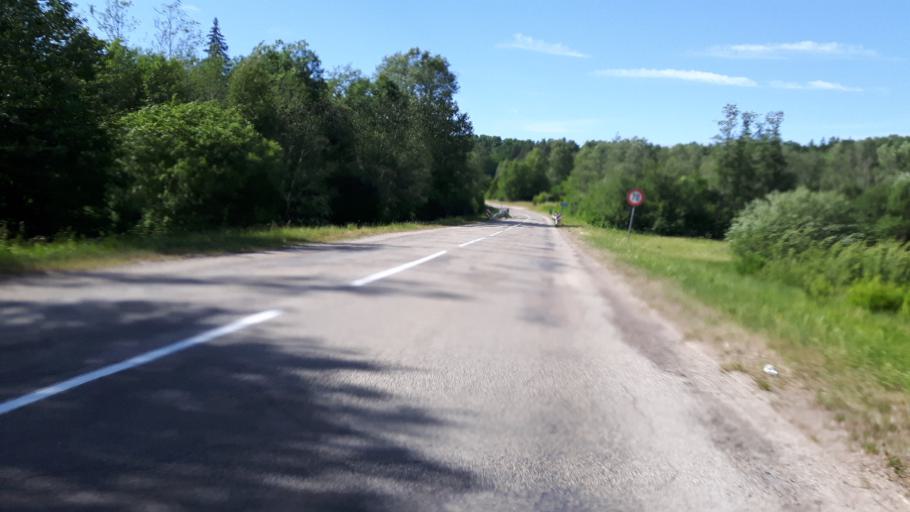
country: LV
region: Talsu Rajons
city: Sabile
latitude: 57.0831
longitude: 22.5257
